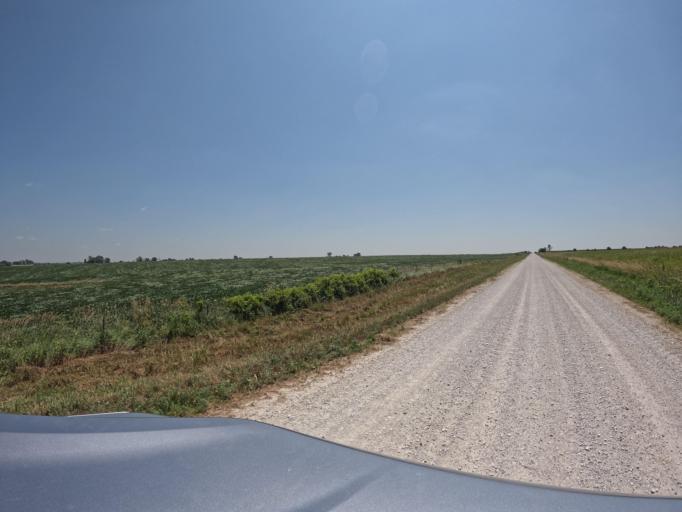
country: US
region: Iowa
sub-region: Keokuk County
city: Sigourney
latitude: 41.2716
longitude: -92.1806
